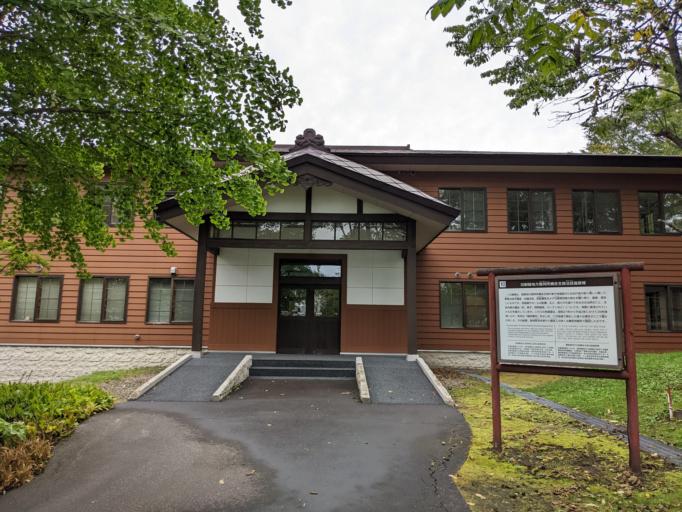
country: JP
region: Hokkaido
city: Abashiri
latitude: 43.9965
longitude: 144.2291
